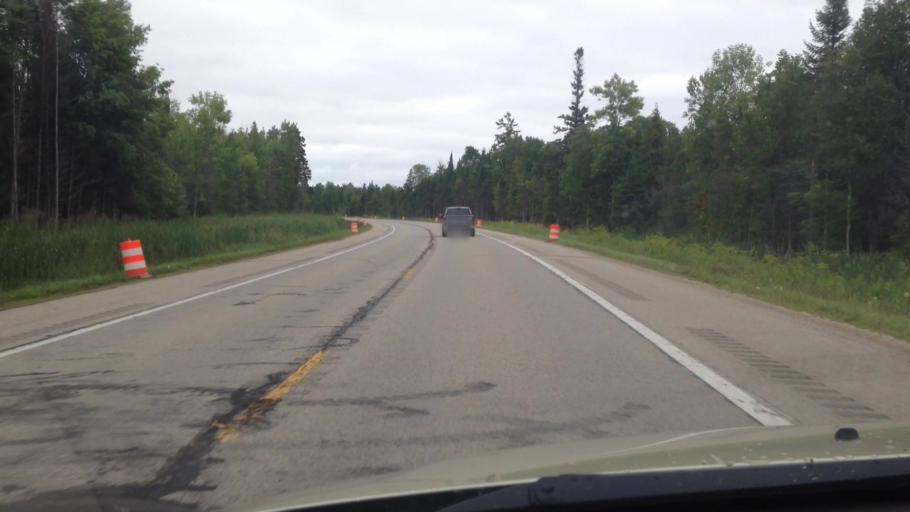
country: US
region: Michigan
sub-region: Delta County
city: Escanaba
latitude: 45.5976
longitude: -87.2281
